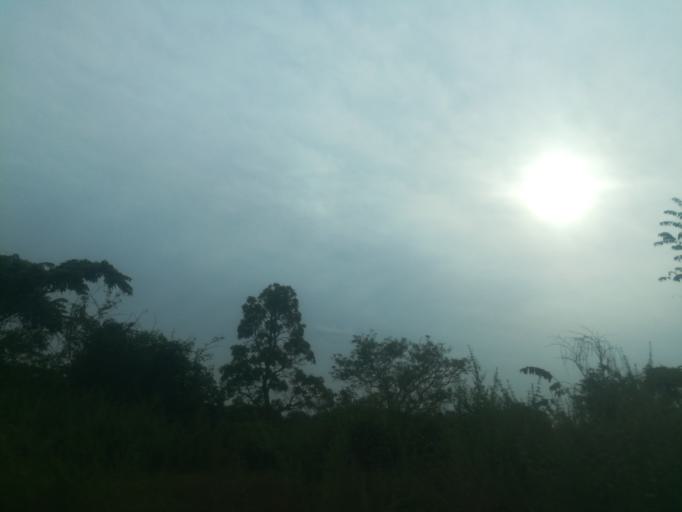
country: NG
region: Ogun
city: Ayetoro
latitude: 7.2718
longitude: 3.1019
